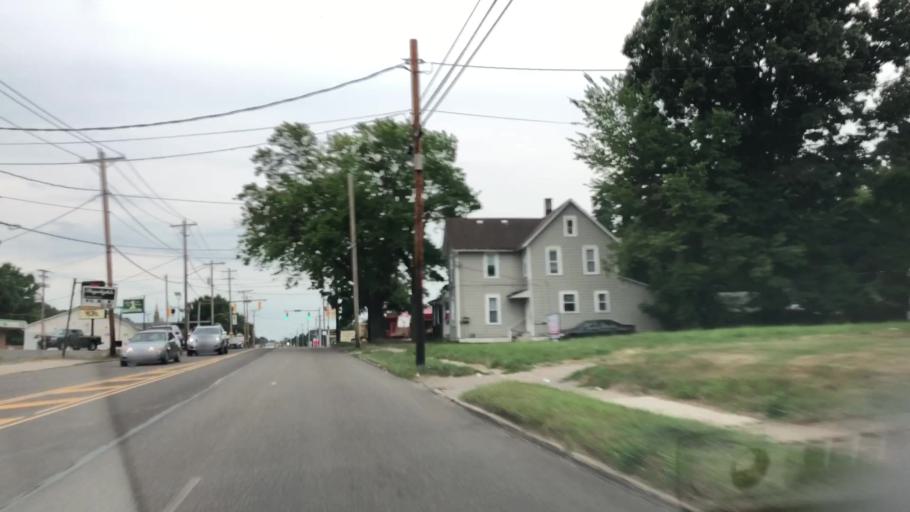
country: US
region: Ohio
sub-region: Stark County
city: North Canton
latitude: 40.8401
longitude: -81.3905
